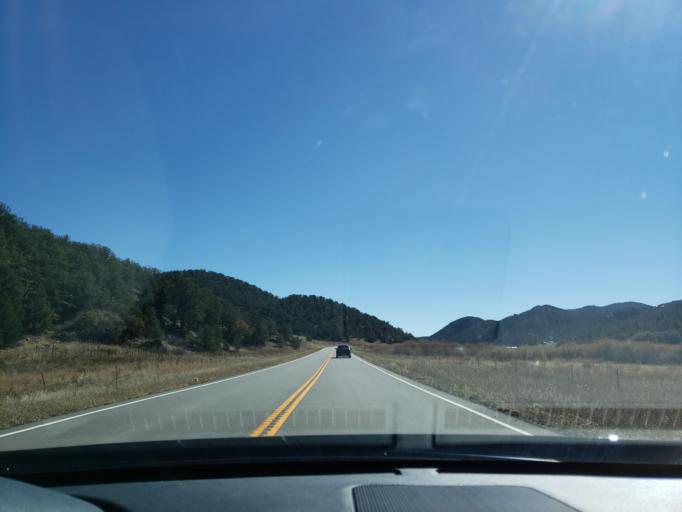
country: US
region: Colorado
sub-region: Fremont County
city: Canon City
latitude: 38.6355
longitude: -105.4651
